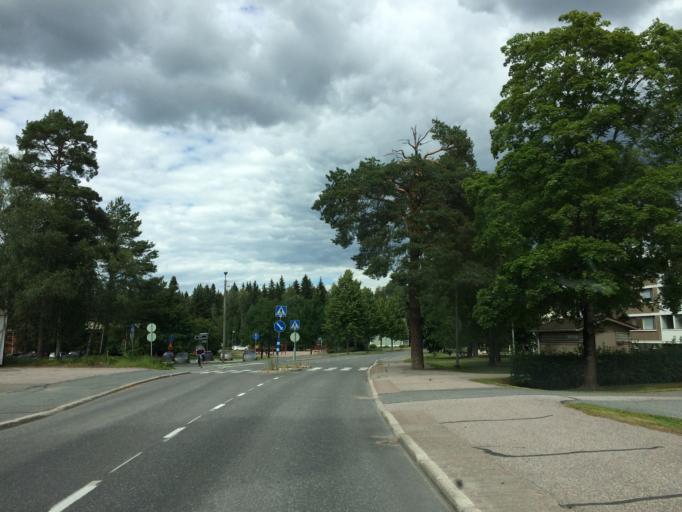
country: FI
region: Haeme
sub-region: Haemeenlinna
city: Tervakoski
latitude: 60.8171
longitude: 24.6227
